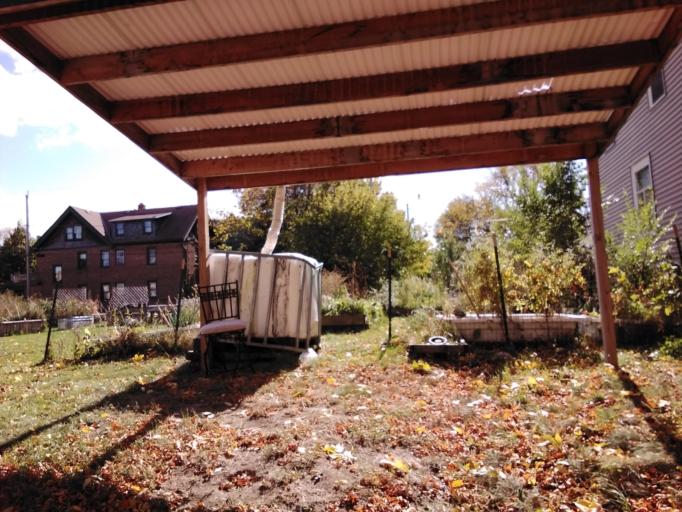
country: US
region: Wisconsin
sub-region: Milwaukee County
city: Milwaukee
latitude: 43.0642
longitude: -87.9493
